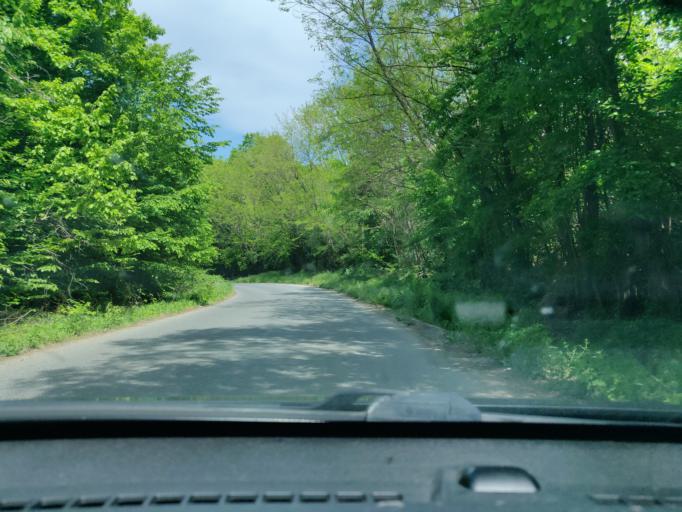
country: RO
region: Vrancea
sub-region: Comuna Vidra
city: Vidra
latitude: 45.9297
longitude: 26.8946
